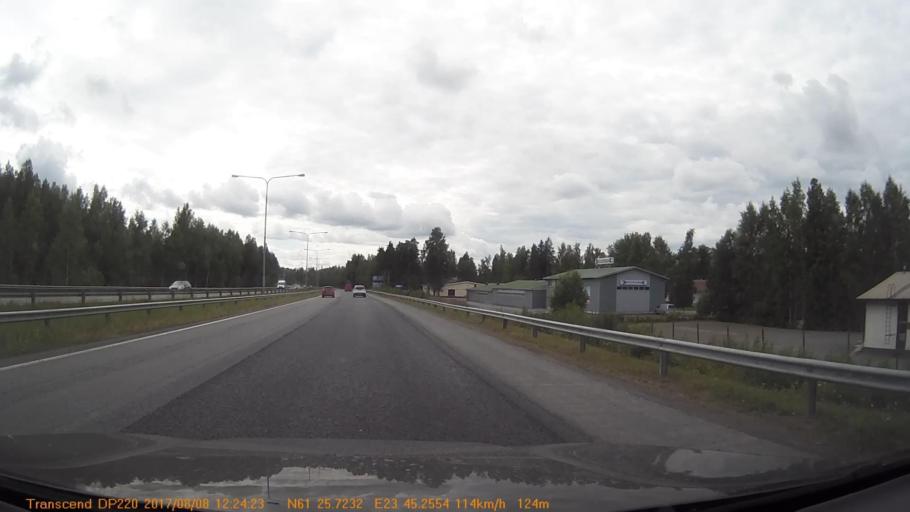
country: FI
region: Pirkanmaa
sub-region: Tampere
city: Tampere
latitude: 61.4287
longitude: 23.7542
